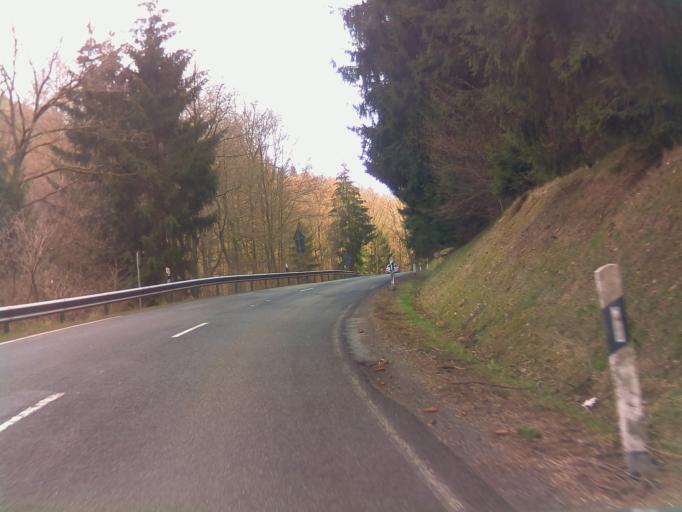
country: DE
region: Rheinland-Pfalz
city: Sensweiler
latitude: 49.7691
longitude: 7.2126
